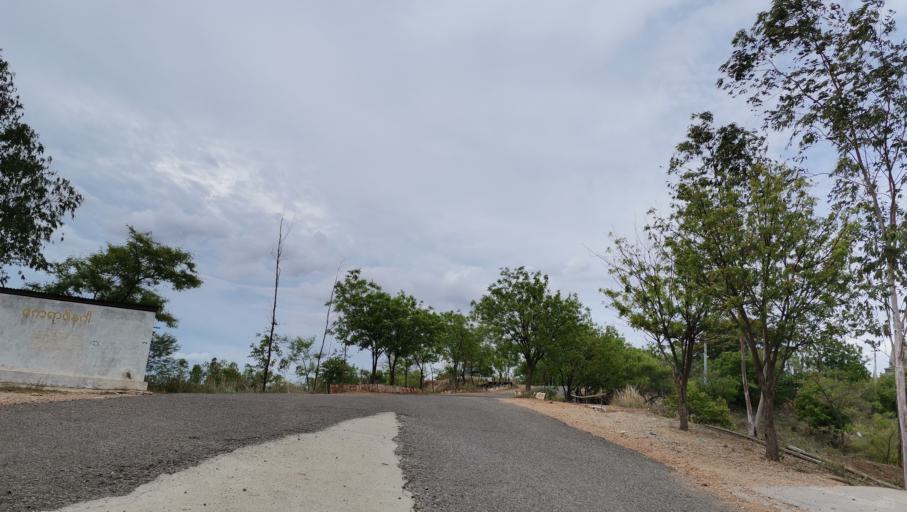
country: MM
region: Mandalay
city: Myingyan
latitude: 21.8249
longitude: 95.3928
